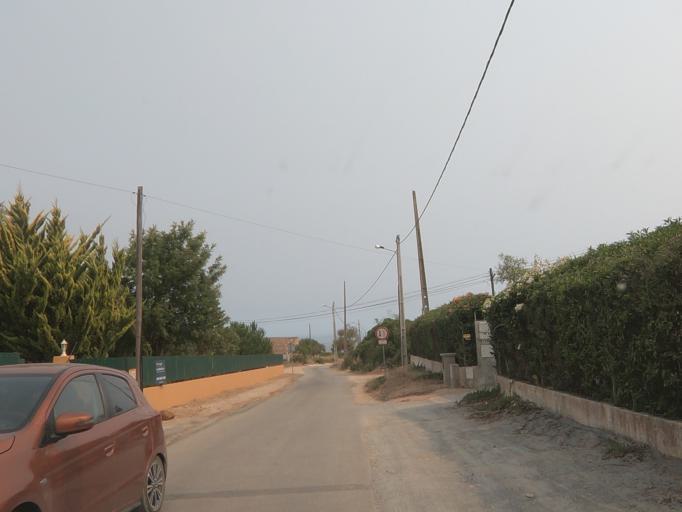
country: PT
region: Faro
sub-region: Lagoa
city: Carvoeiro
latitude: 37.0980
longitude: -8.4104
